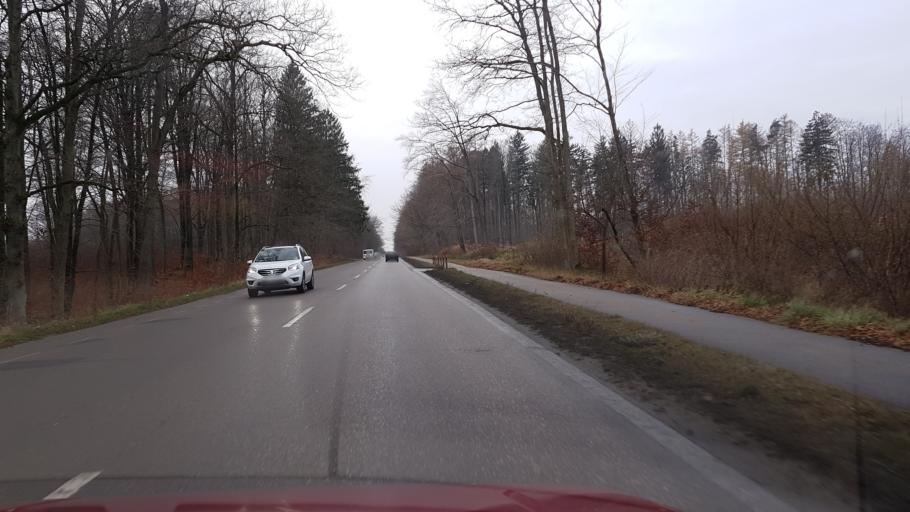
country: PL
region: West Pomeranian Voivodeship
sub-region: Koszalin
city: Koszalin
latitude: 54.2156
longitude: 16.1260
